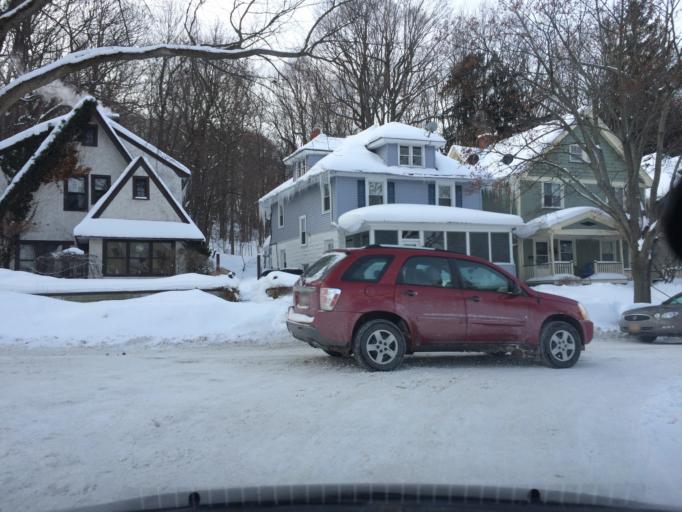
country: US
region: New York
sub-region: Monroe County
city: Rochester
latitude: 43.1363
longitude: -77.5887
